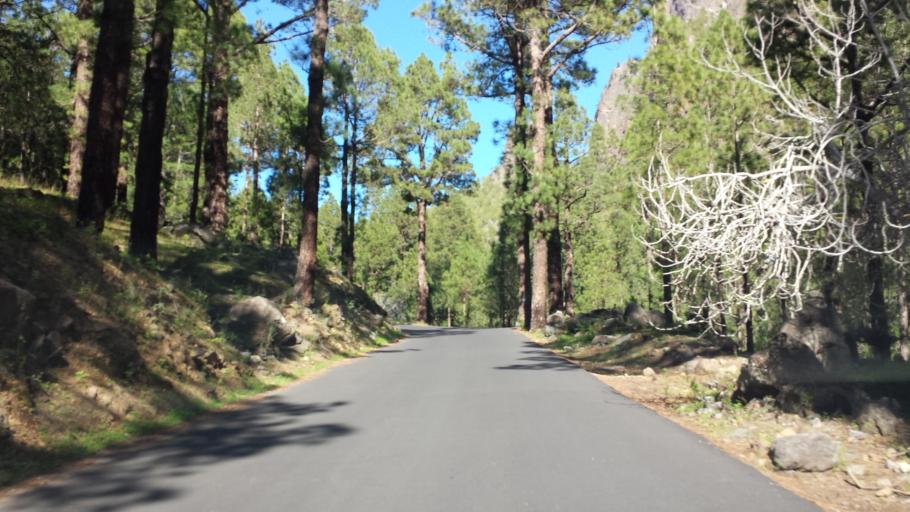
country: ES
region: Canary Islands
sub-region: Provincia de Santa Cruz de Tenerife
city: El Paso
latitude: 28.6890
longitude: -17.8502
